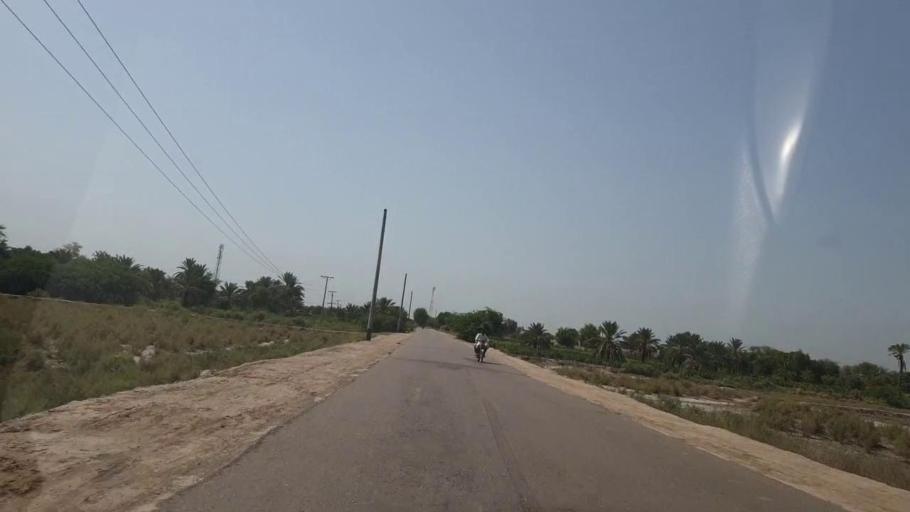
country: PK
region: Sindh
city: Setharja Old
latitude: 27.1263
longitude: 68.5389
